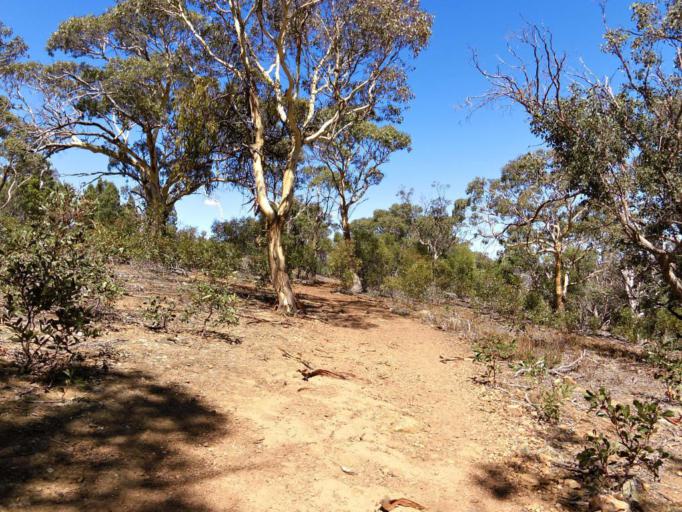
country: AU
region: Victoria
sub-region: Moorabool
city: Bacchus Marsh
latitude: -37.6591
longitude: 144.3534
